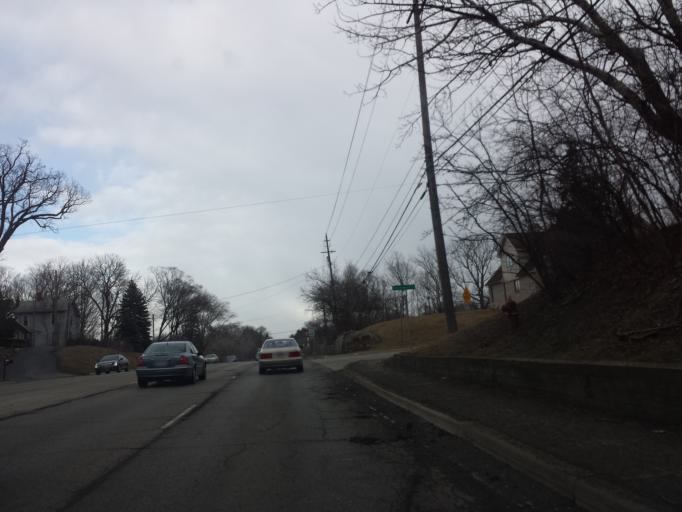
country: US
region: Michigan
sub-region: Oakland County
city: Bingham Farms
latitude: 42.5012
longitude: -83.2772
